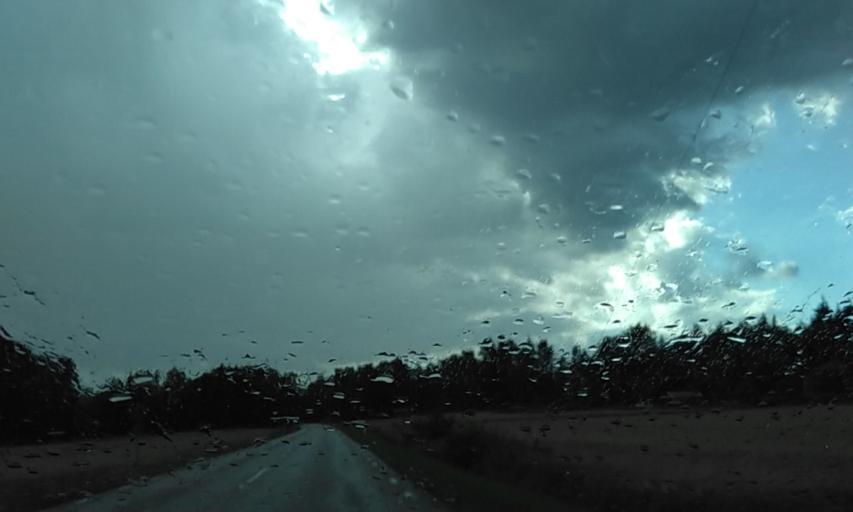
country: SE
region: Vaestra Goetaland
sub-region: Lidkopings Kommun
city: Lidkoping
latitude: 58.5031
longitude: 12.9725
